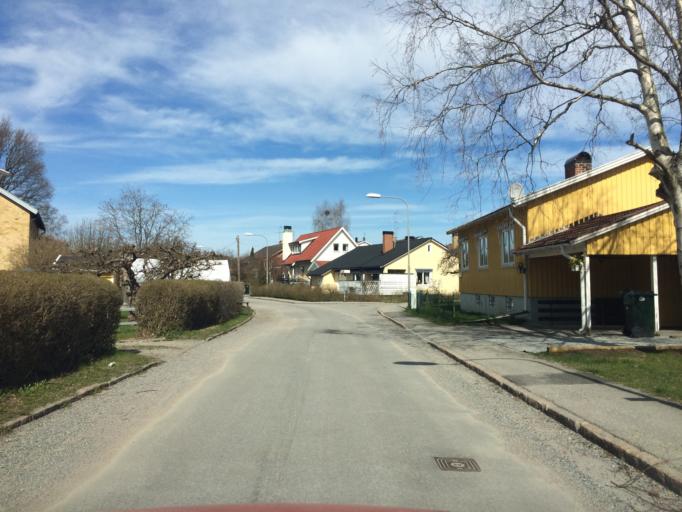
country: SE
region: Stockholm
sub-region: Huddinge Kommun
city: Huddinge
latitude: 59.2842
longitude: 17.9805
